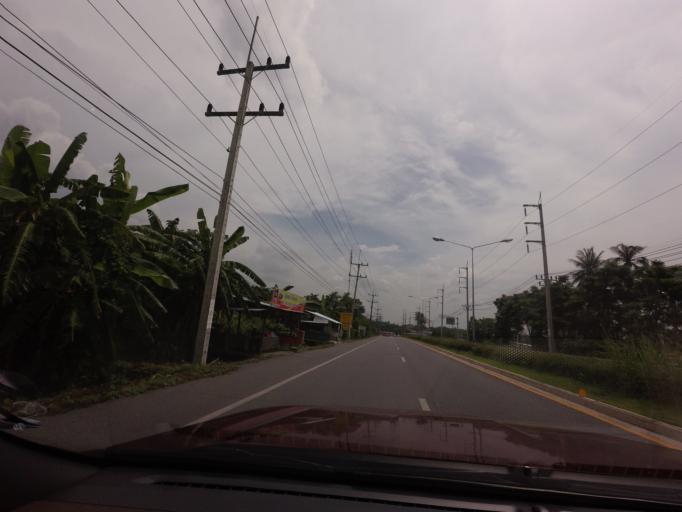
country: TH
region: Yala
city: Yala
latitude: 6.5011
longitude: 101.2705
